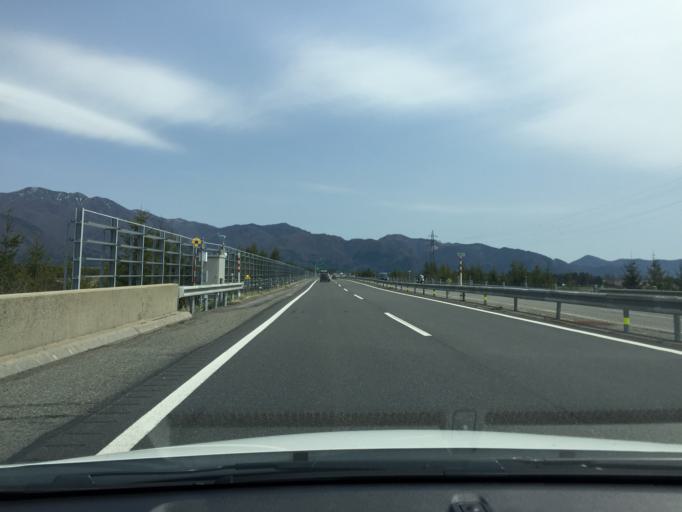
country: JP
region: Fukushima
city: Inawashiro
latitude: 37.5453
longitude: 140.0967
